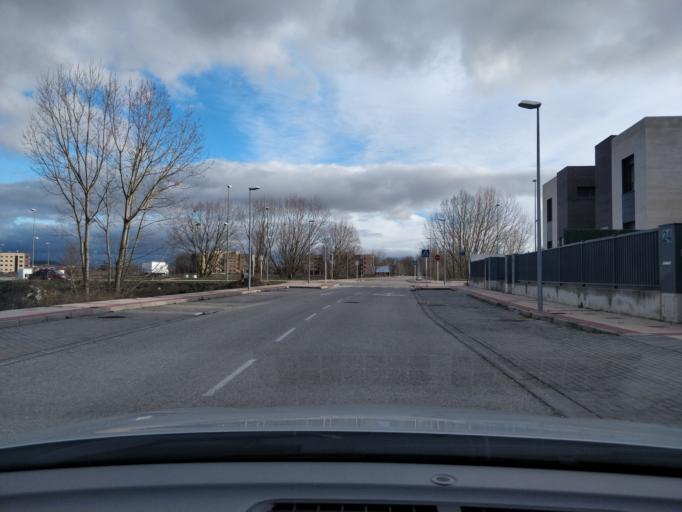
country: ES
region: Castille and Leon
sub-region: Provincia de Burgos
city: Villalbilla de Burgos
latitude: 42.3550
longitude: -3.7611
